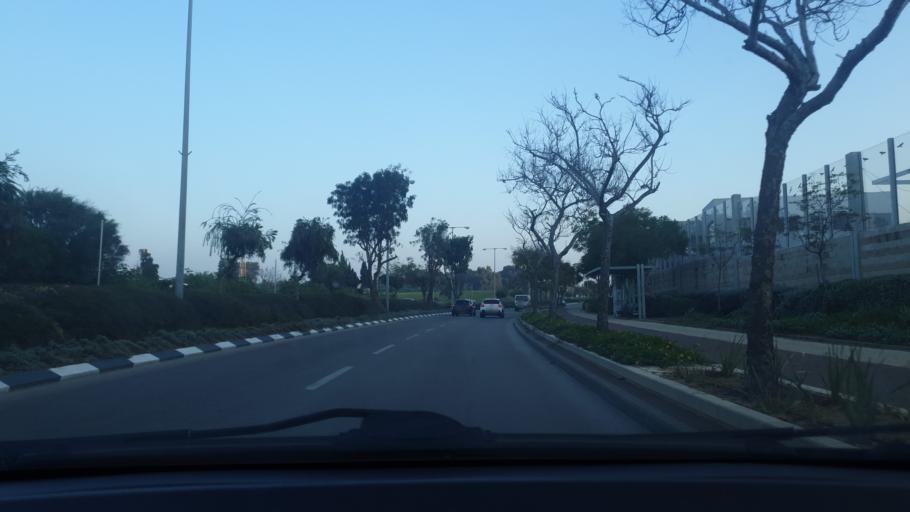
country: IL
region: Central District
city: Bet Dagan
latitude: 31.9705
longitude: 34.8249
